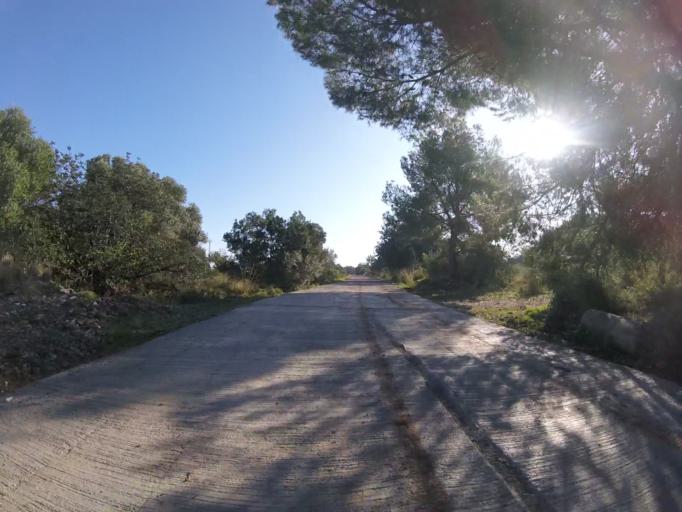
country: ES
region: Valencia
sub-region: Provincia de Castello
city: Peniscola
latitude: 40.3900
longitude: 0.3694
